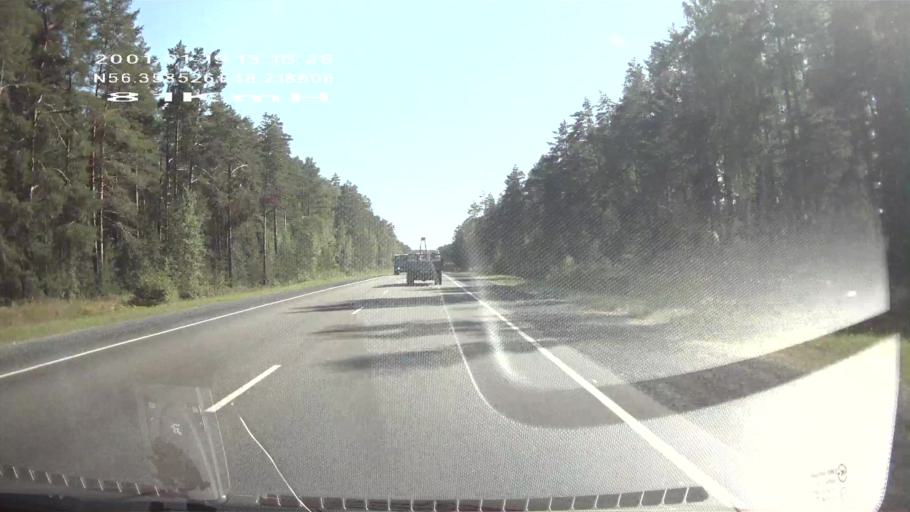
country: RU
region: Mariy-El
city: Suslonger
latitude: 56.3584
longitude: 48.2187
